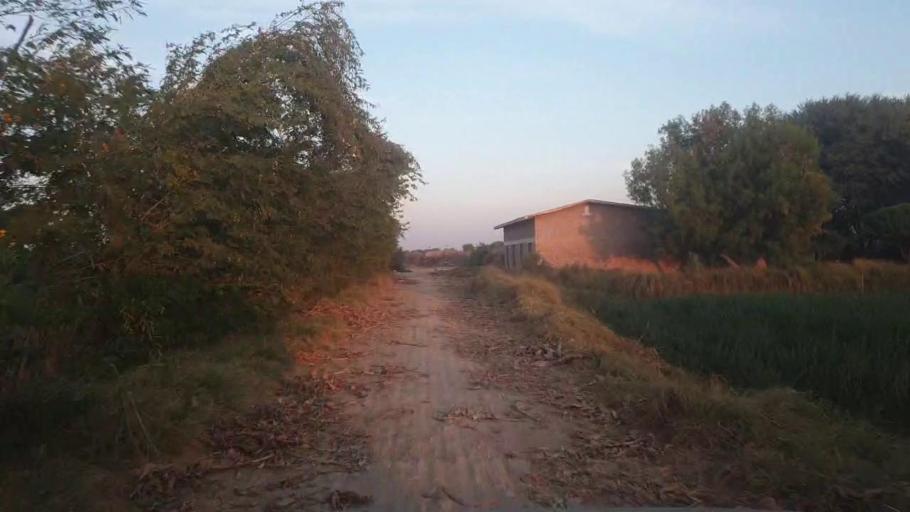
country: PK
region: Sindh
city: Hala
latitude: 25.6965
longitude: 68.3203
